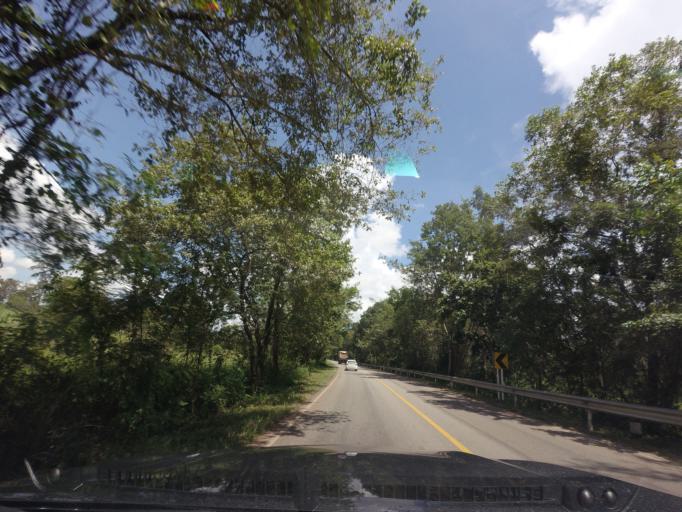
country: TH
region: Changwat Udon Thani
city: Phibun Rak
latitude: 17.5821
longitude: 103.0377
